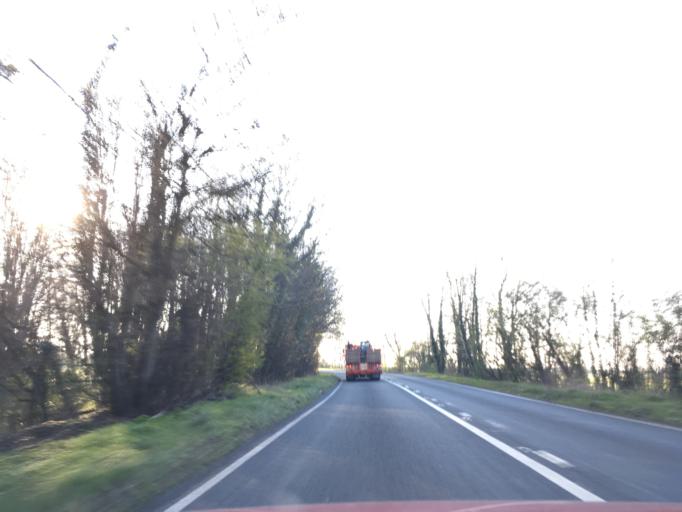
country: GB
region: England
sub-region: Gloucestershire
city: Bourton on the Water
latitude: 51.8072
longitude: -1.7143
